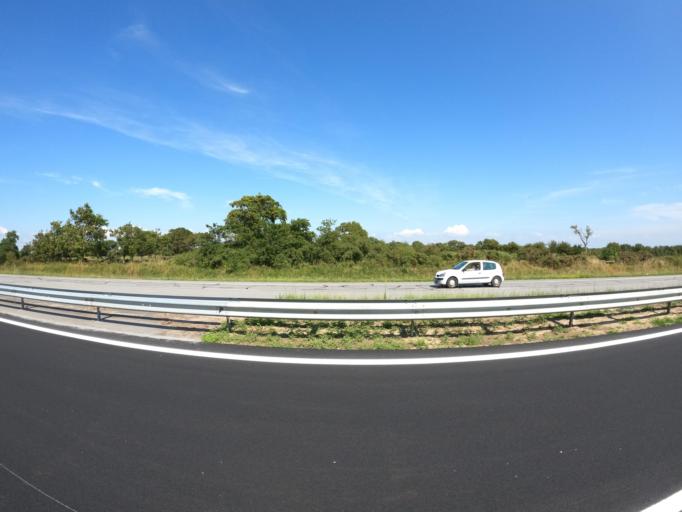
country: FR
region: Pays de la Loire
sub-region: Departement de la Loire-Atlantique
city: Saint-Michel-Chef-Chef
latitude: 47.1725
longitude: -2.1444
